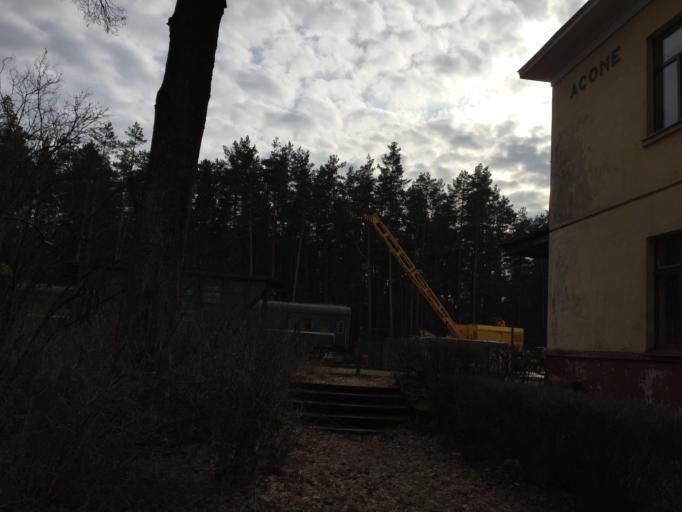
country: LV
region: Stopini
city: Ulbroka
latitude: 56.9212
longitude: 24.2994
